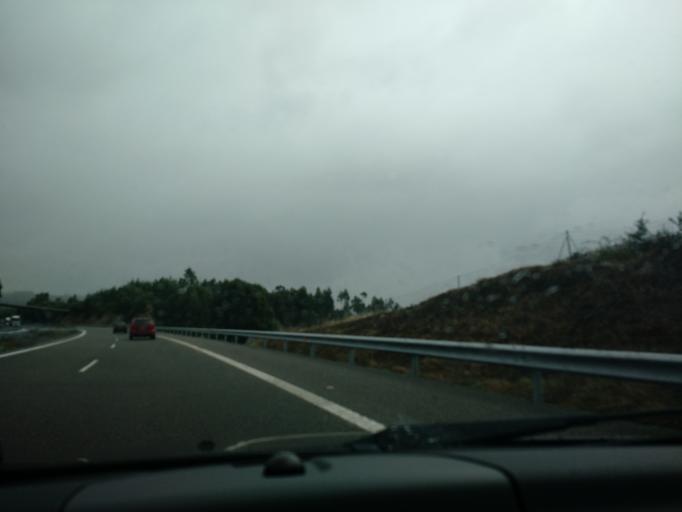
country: ES
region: Galicia
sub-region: Provincia da Coruna
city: Mesia
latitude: 43.1256
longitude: -8.3276
